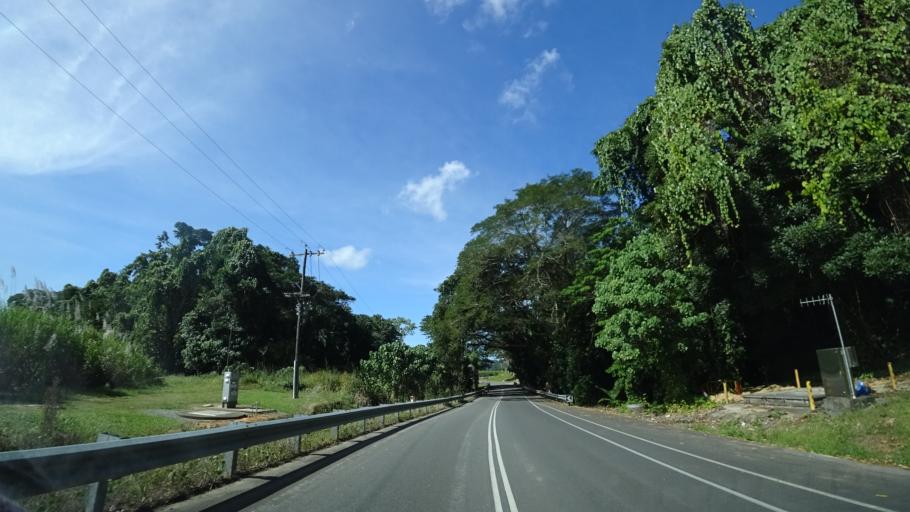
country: AU
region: Queensland
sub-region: Cairns
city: Port Douglas
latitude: -16.4669
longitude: 145.3635
